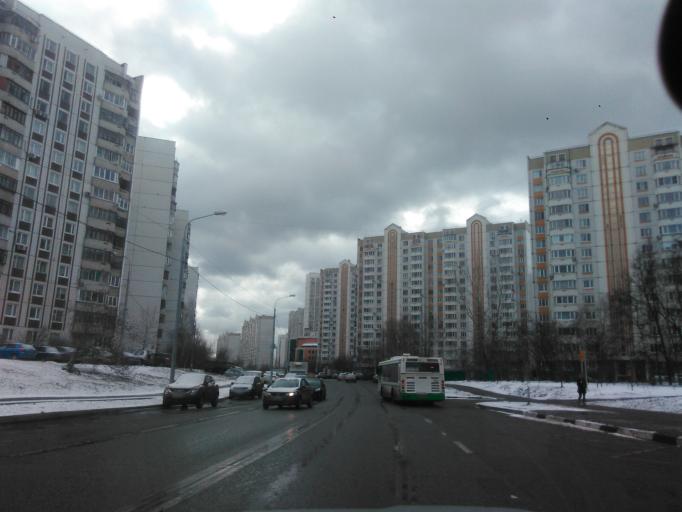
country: RU
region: Moskovskaya
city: Krasnogorsk
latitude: 55.8483
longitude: 37.3438
